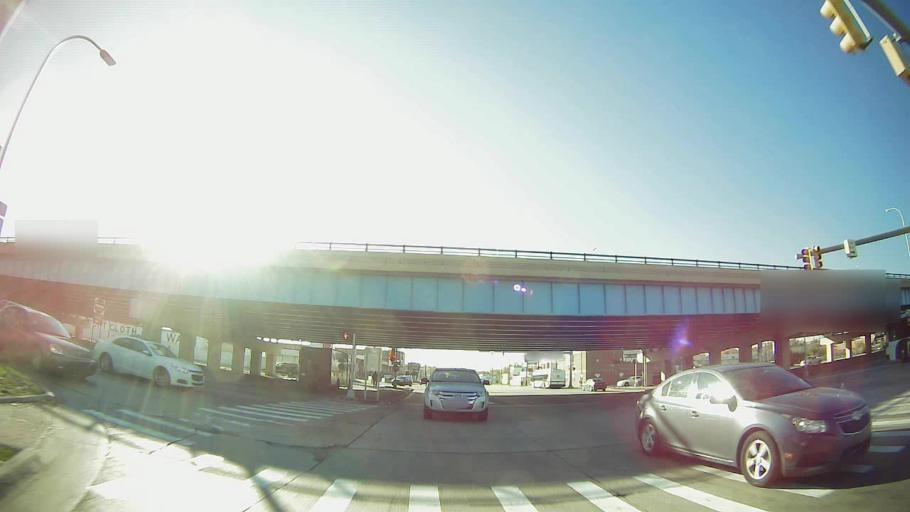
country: US
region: Michigan
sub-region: Oakland County
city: Oak Park
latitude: 42.4452
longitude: -83.2004
